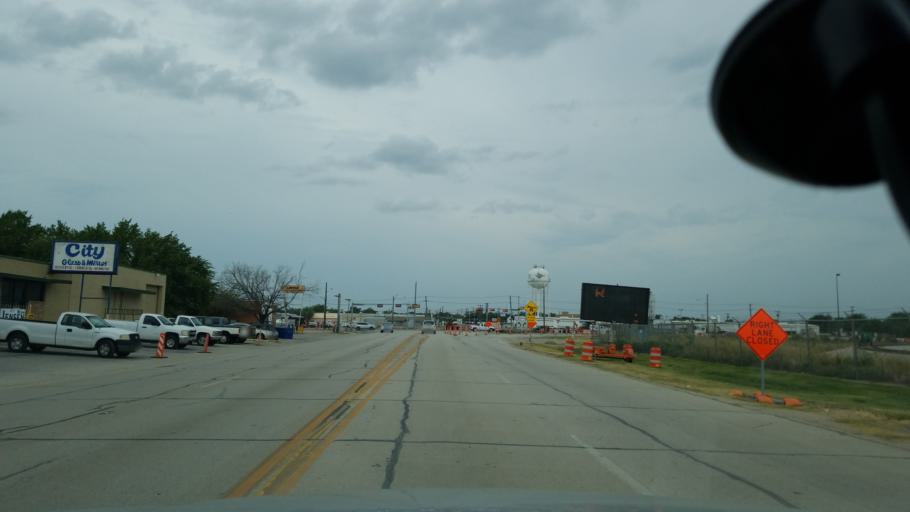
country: US
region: Texas
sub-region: Dallas County
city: Grand Prairie
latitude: 32.7436
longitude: -96.9877
